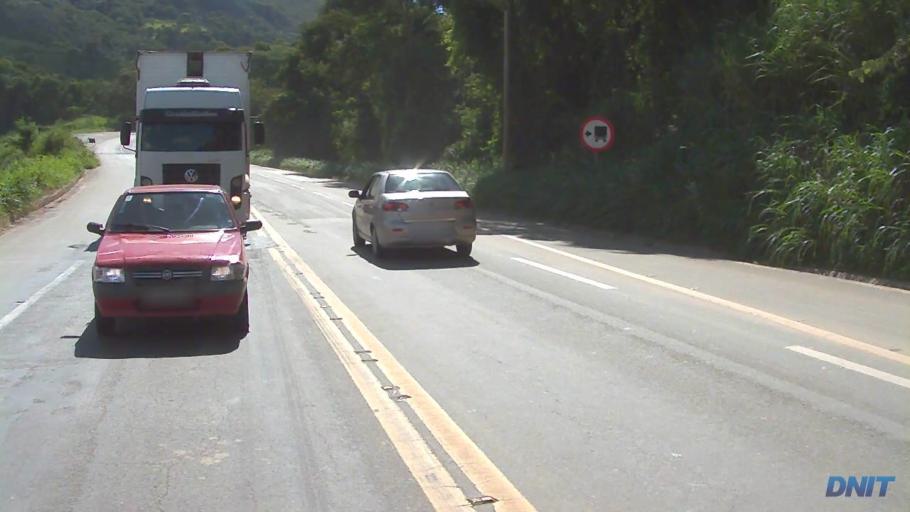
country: BR
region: Minas Gerais
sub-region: Caete
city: Caete
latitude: -19.7487
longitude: -43.5221
